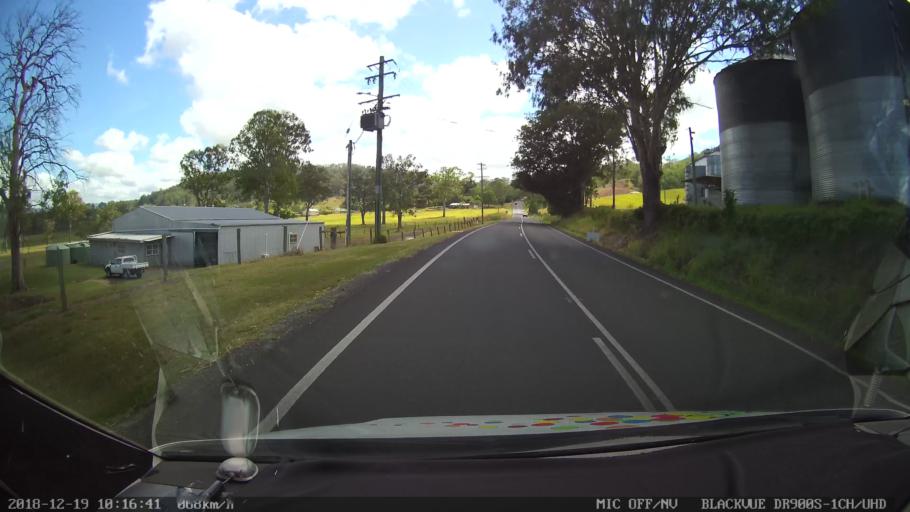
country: AU
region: New South Wales
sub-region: Kyogle
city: Kyogle
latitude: -28.6066
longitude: 153.0239
